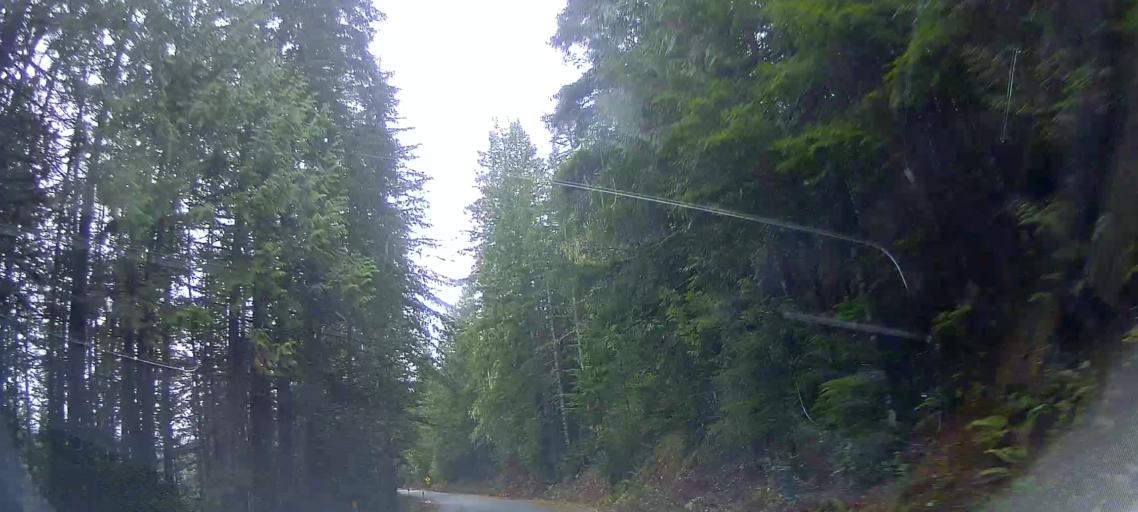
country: US
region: Washington
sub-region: Snohomish County
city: Darrington
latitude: 48.5257
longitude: -121.3873
